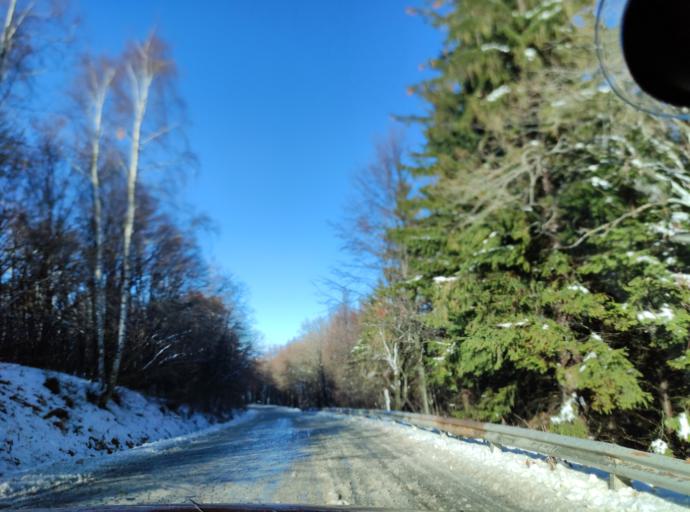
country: BG
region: Sofia-Capital
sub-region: Stolichna Obshtina
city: Sofia
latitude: 42.6040
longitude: 23.3079
